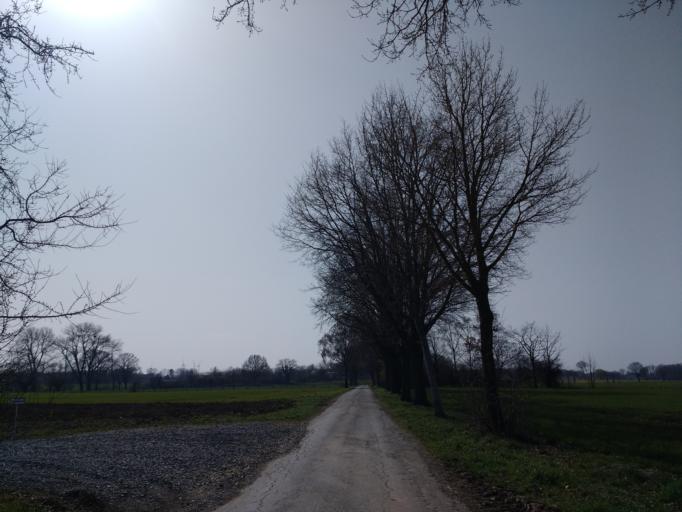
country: DE
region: North Rhine-Westphalia
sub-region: Regierungsbezirk Detmold
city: Salzkotten
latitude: 51.7334
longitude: 8.6545
